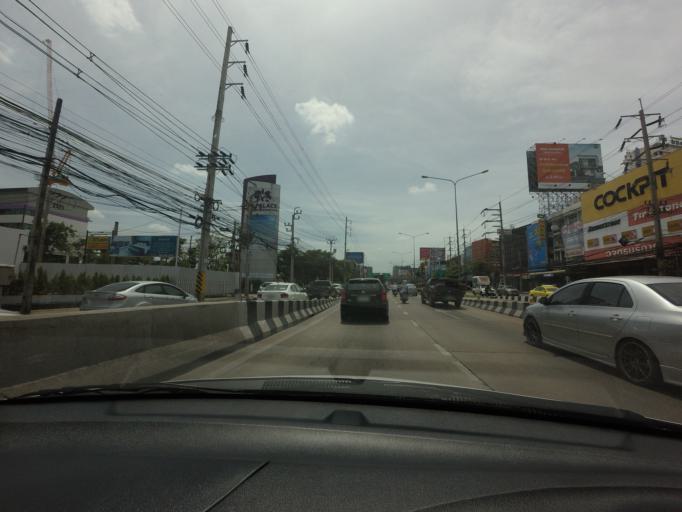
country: TH
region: Bangkok
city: Lak Si
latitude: 13.8926
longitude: 100.5619
